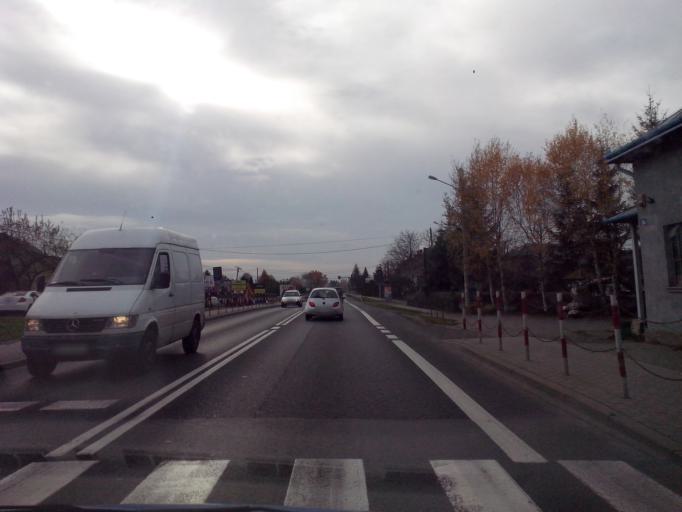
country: PL
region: Subcarpathian Voivodeship
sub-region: Powiat rzeszowski
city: Boguchwala
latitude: 50.0085
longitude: 21.9636
